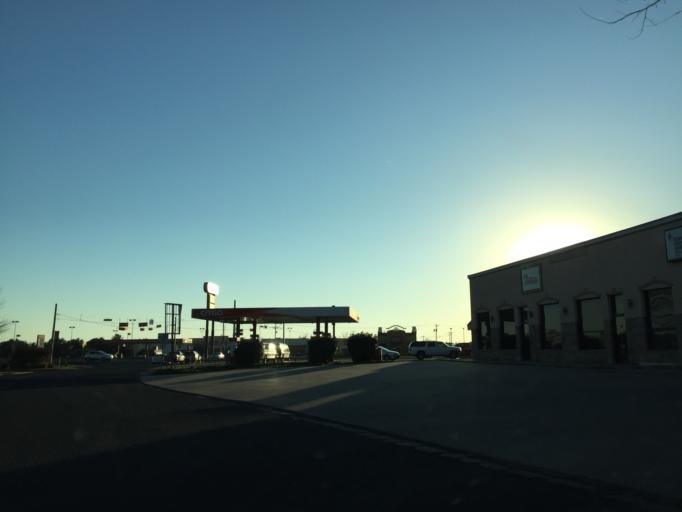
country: US
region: Texas
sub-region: Bastrop County
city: Elgin
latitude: 30.3483
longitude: -97.3824
